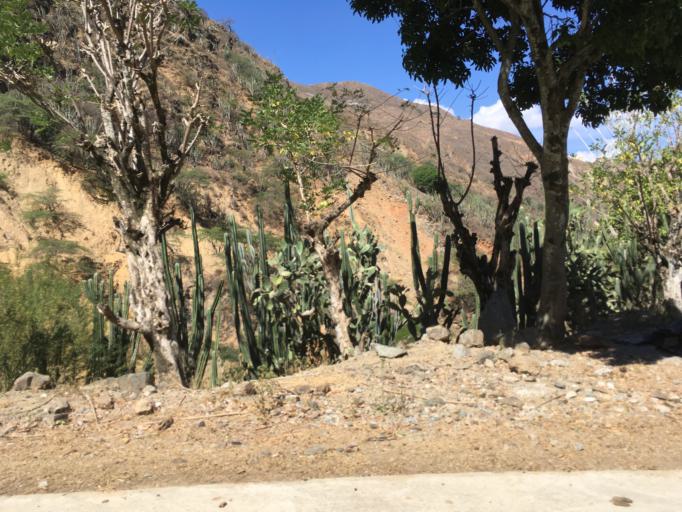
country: CO
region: Santander
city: Aratoca
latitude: 6.7718
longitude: -72.9935
